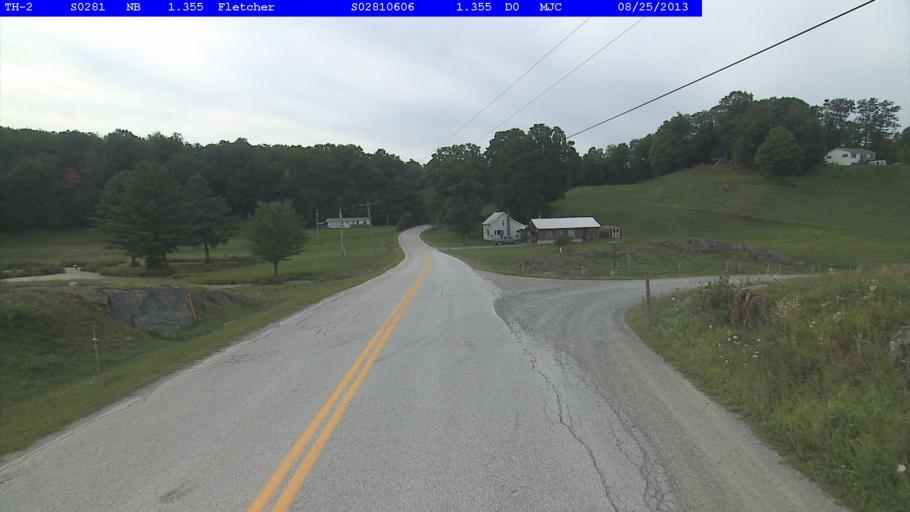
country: US
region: Vermont
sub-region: Chittenden County
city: Milton
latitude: 44.6951
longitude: -72.9336
